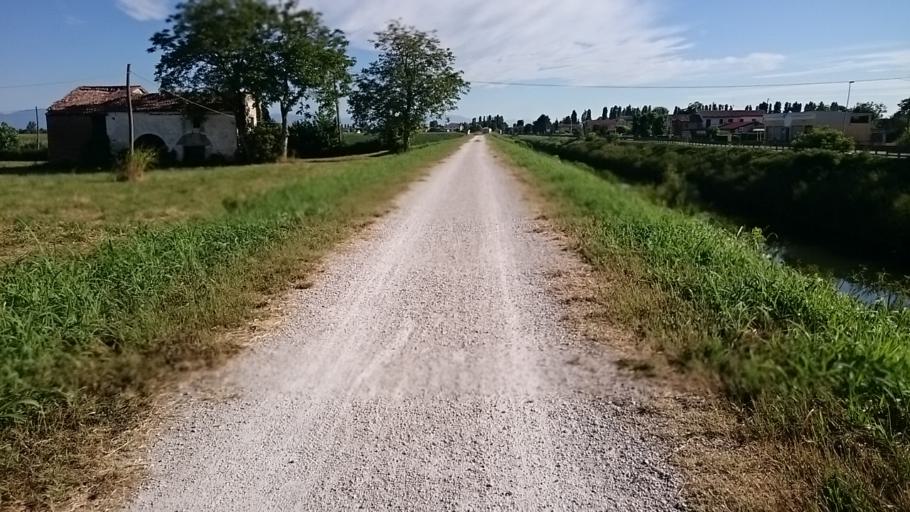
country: IT
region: Veneto
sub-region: Provincia di Padova
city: Campodarsego
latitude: 45.5234
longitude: 11.9144
